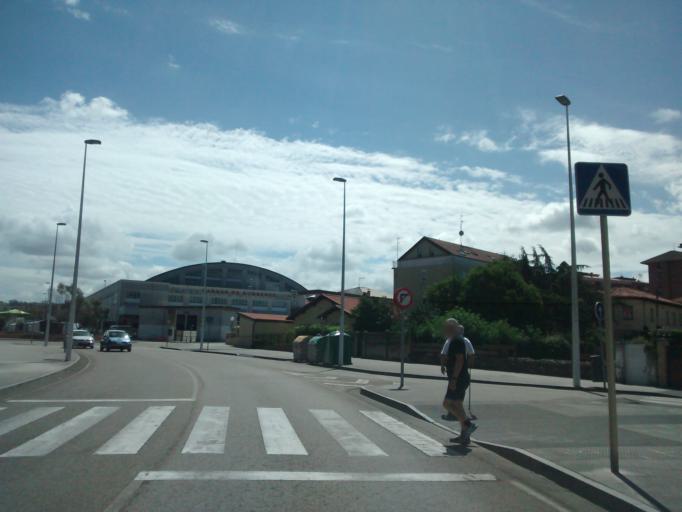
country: ES
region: Cantabria
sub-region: Provincia de Cantabria
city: Torrelavega
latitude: 43.3450
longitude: -4.0538
